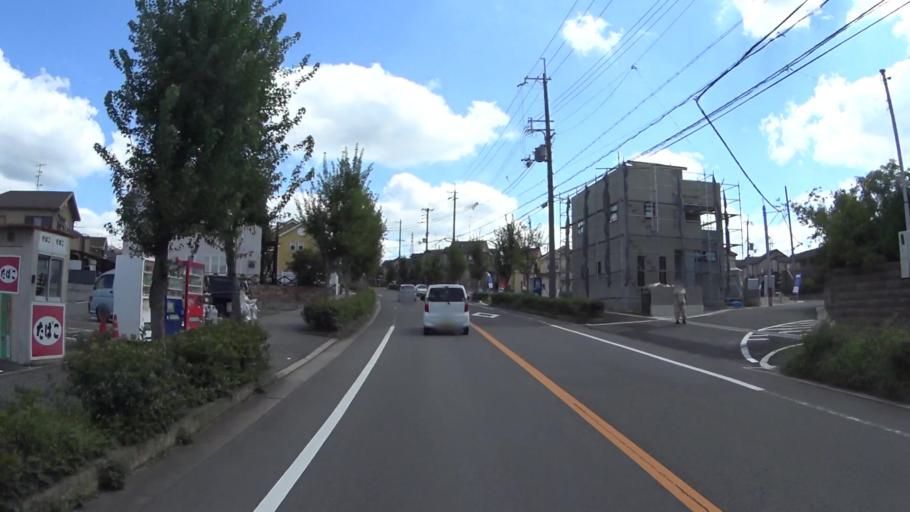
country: JP
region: Kyoto
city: Uji
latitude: 34.8697
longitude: 135.7886
